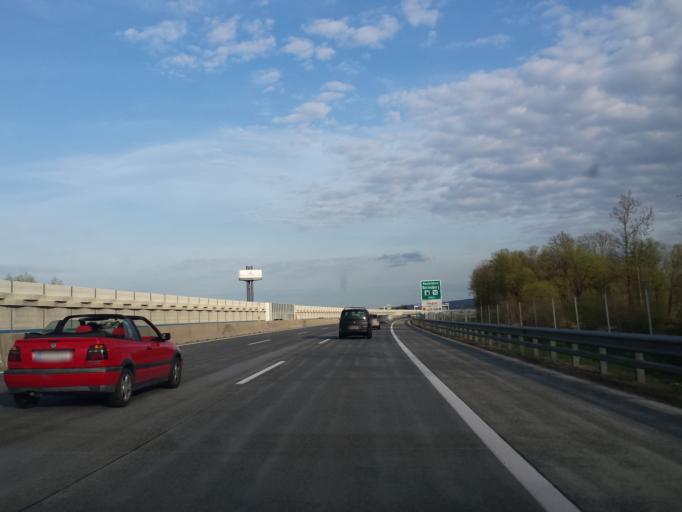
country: AT
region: Lower Austria
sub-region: Politischer Bezirk Korneuburg
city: Leobendorf
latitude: 48.3693
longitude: 16.2923
